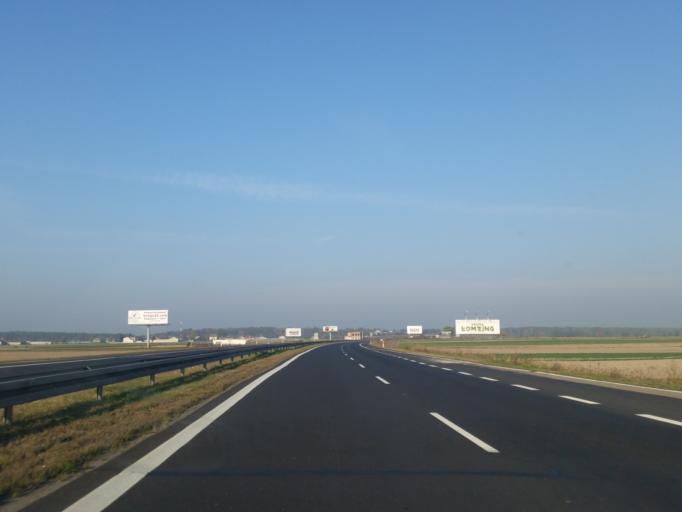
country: PL
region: Masovian Voivodeship
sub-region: Powiat nowodworski
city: Zakroczym
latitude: 52.4458
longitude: 20.6078
